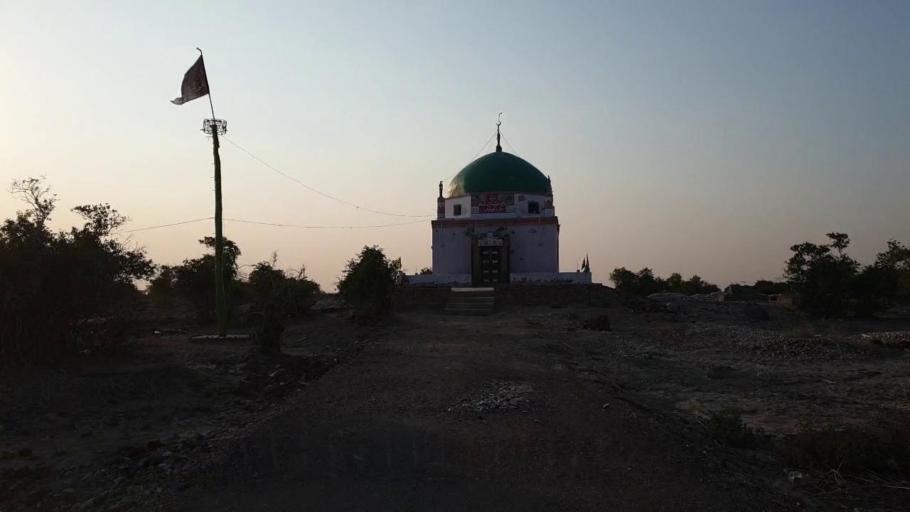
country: PK
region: Sindh
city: Sehwan
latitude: 26.4343
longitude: 67.7638
